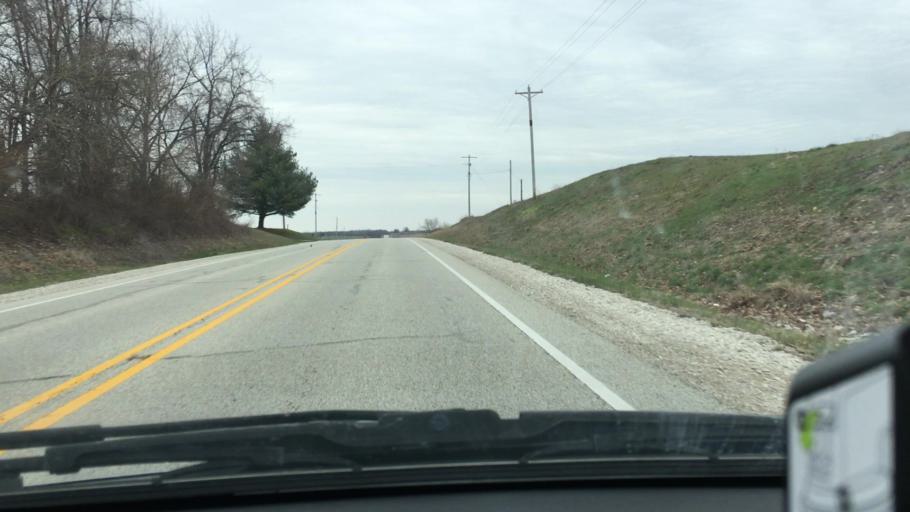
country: US
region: Indiana
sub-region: Greene County
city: Bloomfield
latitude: 38.9951
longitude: -87.0163
